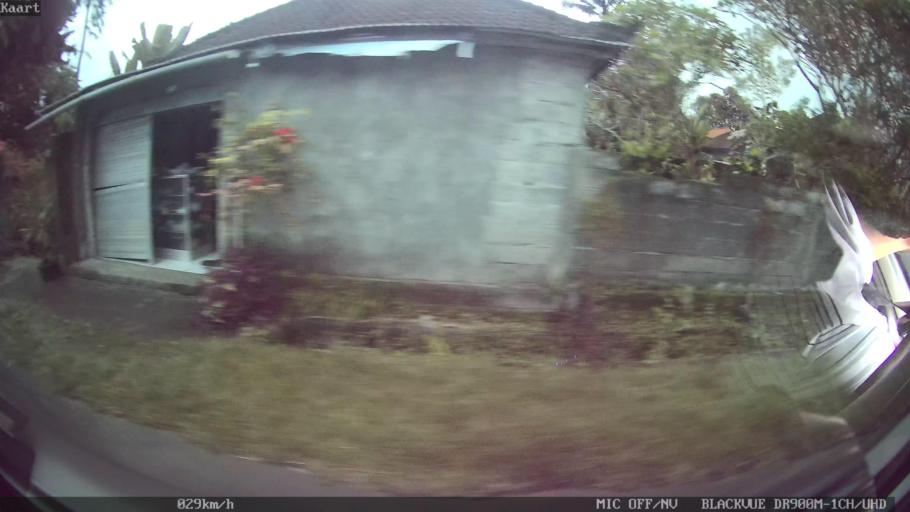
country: ID
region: Bali
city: Petang
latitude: -8.4156
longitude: 115.2243
